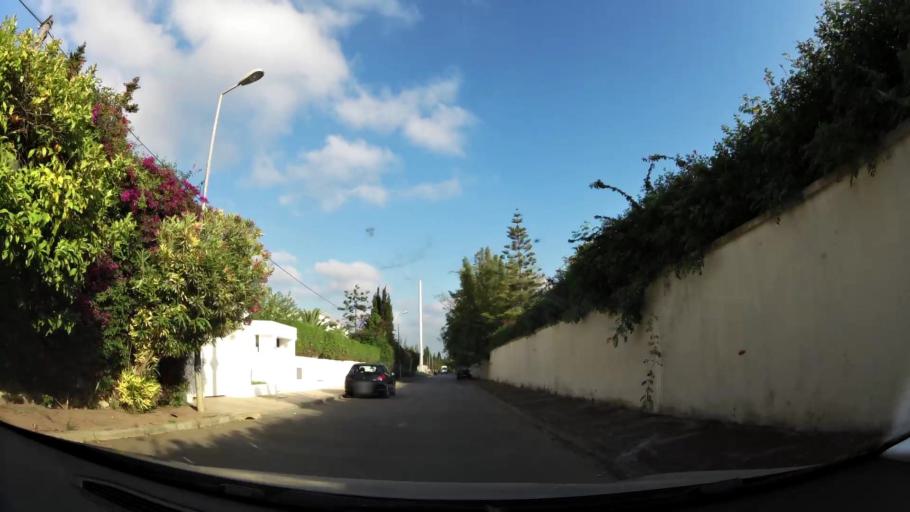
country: MA
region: Rabat-Sale-Zemmour-Zaer
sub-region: Rabat
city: Rabat
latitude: 33.9623
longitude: -6.8453
